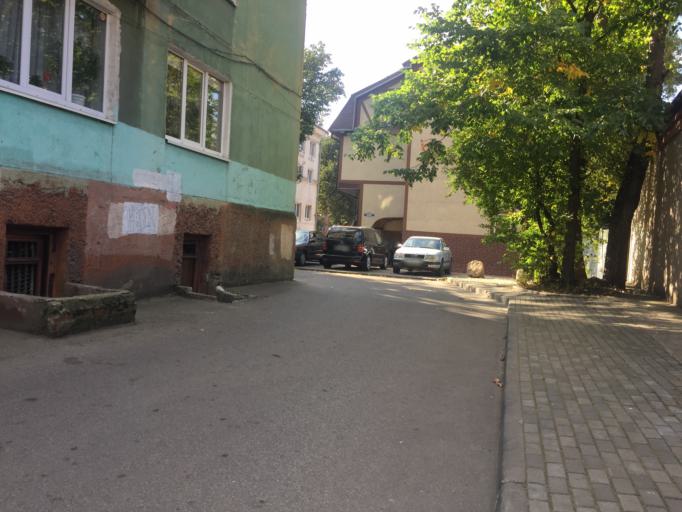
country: RU
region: Kaliningrad
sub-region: Gorod Kaliningrad
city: Kaliningrad
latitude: 54.6985
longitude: 20.5088
